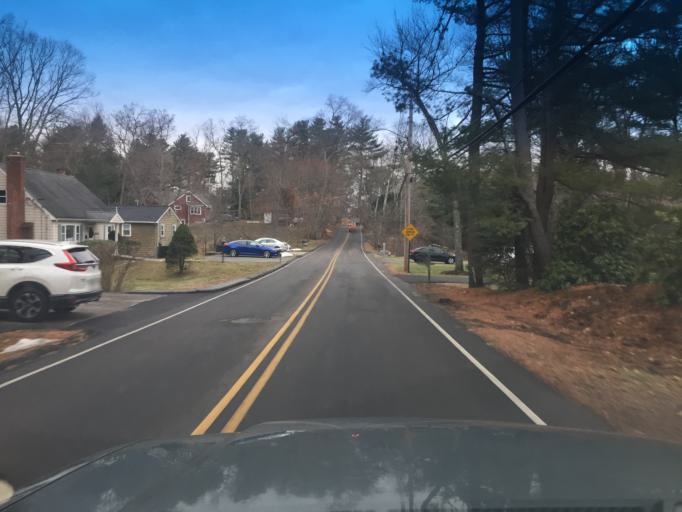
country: US
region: Massachusetts
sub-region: Norfolk County
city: Millis
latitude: 42.1764
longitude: -71.3654
